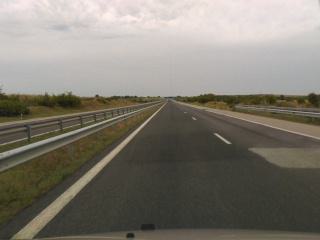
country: BG
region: Stara Zagora
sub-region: Obshtina Chirpan
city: Chirpan
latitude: 42.2472
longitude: 25.3992
